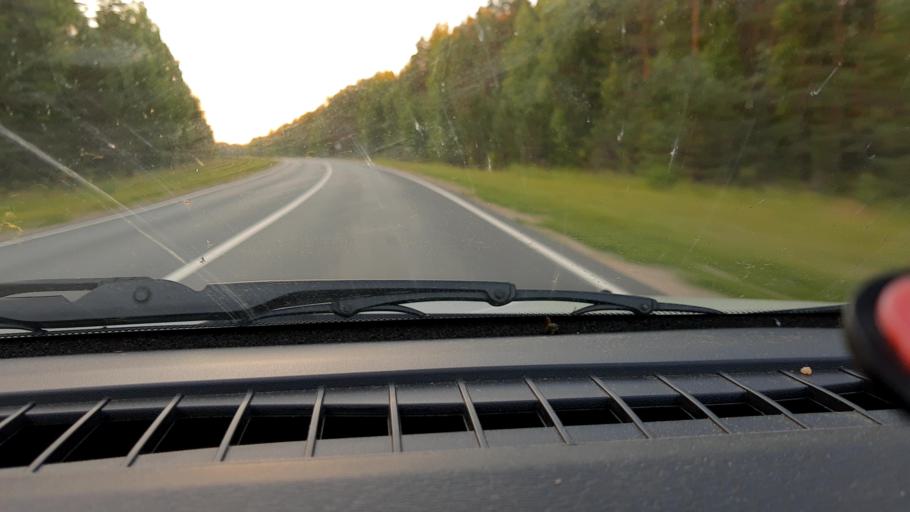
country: RU
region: Nizjnij Novgorod
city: Krasnyye Baki
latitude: 57.2042
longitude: 45.4604
